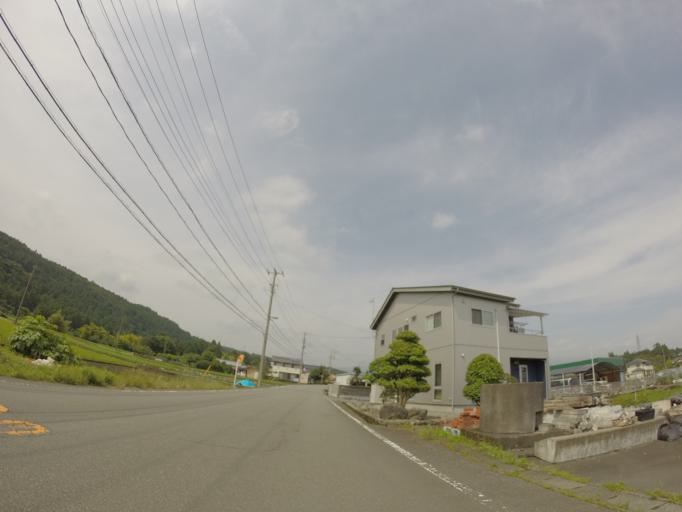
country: JP
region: Shizuoka
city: Fujinomiya
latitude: 35.2898
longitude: 138.5784
